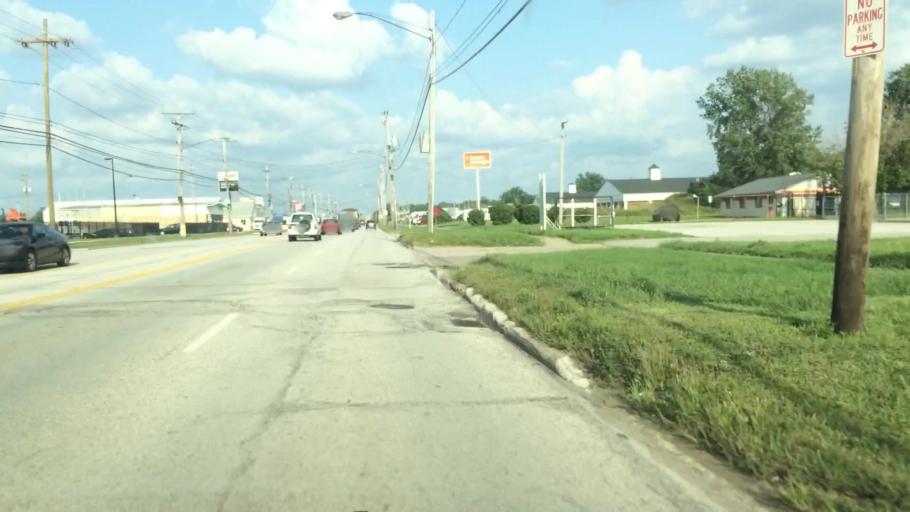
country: US
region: Ohio
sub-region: Cuyahoga County
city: Parma Heights
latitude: 41.4184
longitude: -81.7668
